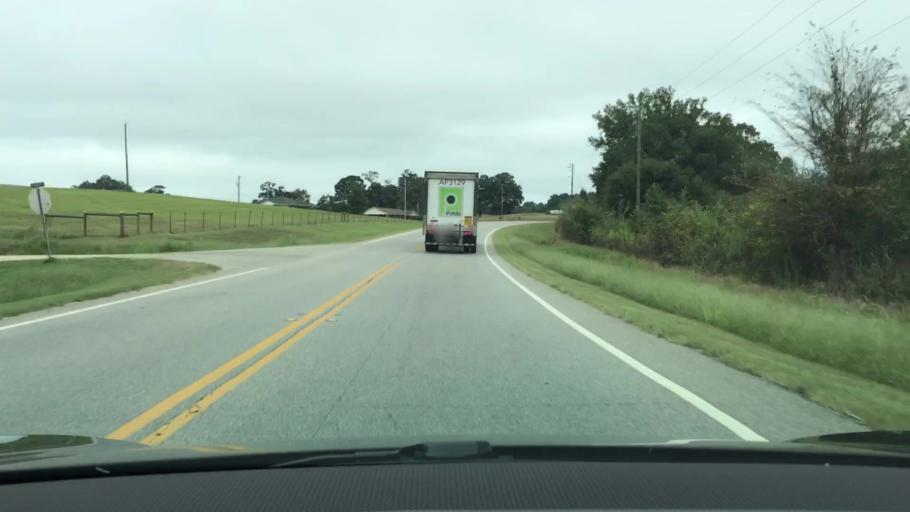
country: US
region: Georgia
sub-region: Greene County
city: Greensboro
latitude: 33.6443
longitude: -83.2311
